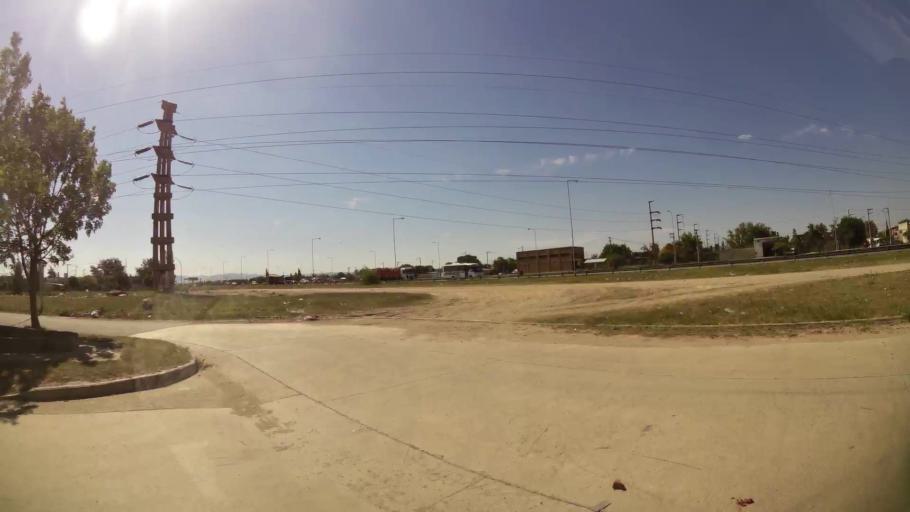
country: AR
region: Cordoba
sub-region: Departamento de Capital
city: Cordoba
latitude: -31.3621
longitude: -64.1530
